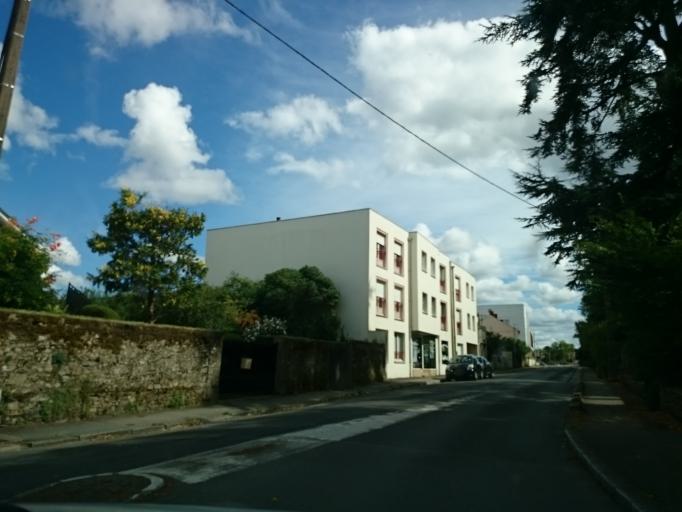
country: FR
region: Pays de la Loire
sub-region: Departement de la Loire-Atlantique
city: Reze
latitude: 47.1898
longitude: -1.5684
